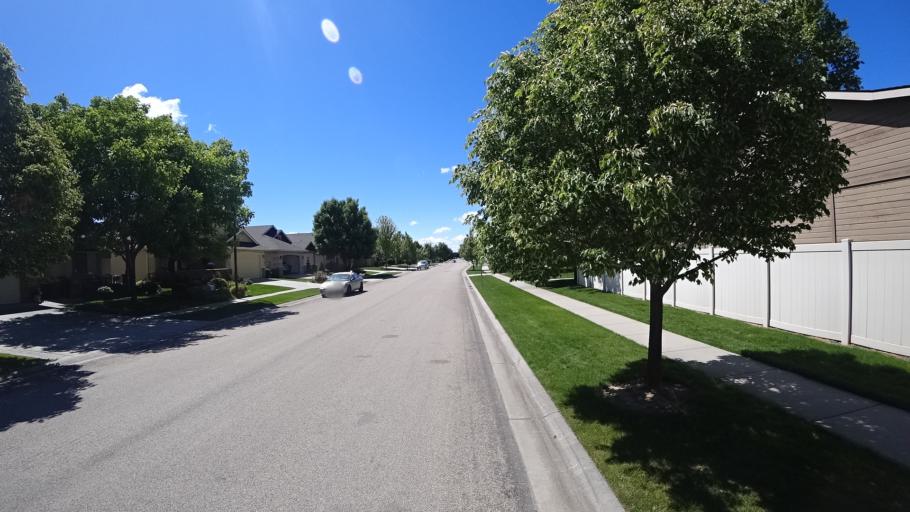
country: US
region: Idaho
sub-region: Ada County
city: Eagle
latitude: 43.6608
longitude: -116.3825
